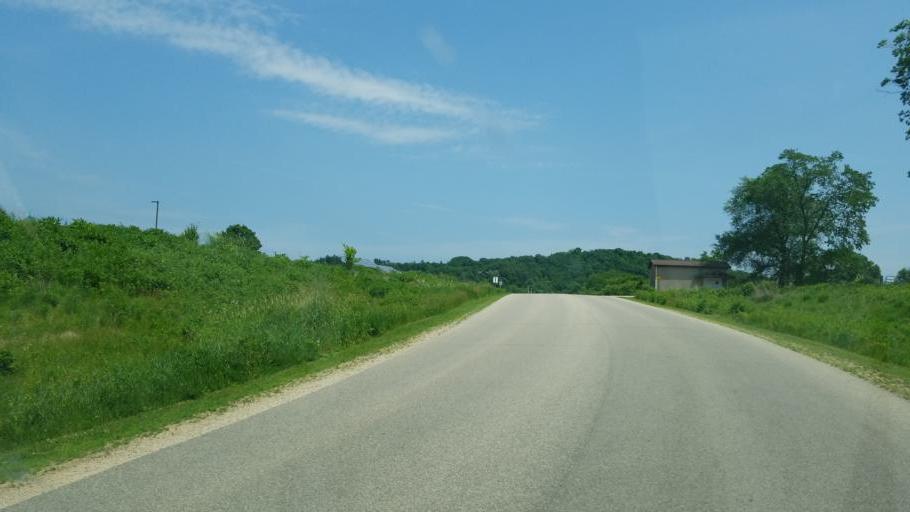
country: US
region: Wisconsin
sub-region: Monroe County
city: Cashton
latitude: 43.5818
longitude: -90.6381
